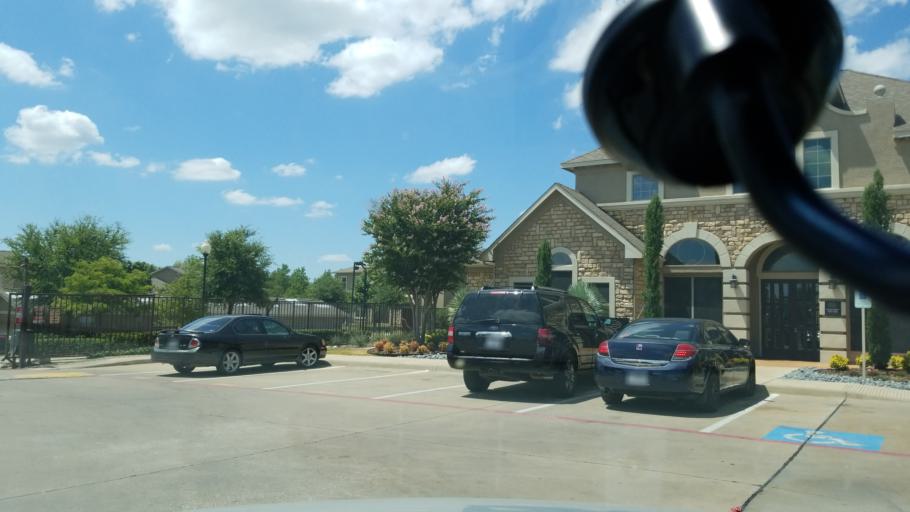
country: US
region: Texas
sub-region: Dallas County
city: Cockrell Hill
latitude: 32.6957
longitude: -96.8249
